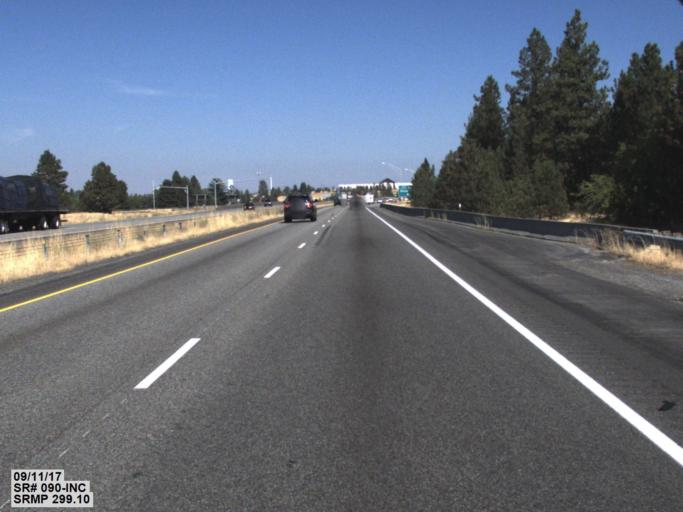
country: US
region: Washington
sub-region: Spokane County
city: Otis Orchards-East Farms
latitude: 47.6932
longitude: -117.0561
